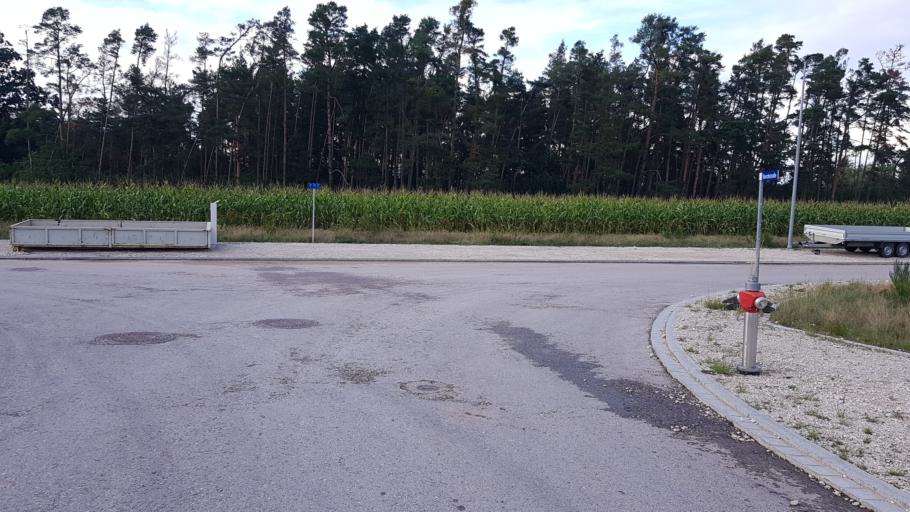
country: DE
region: Bavaria
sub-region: Regierungsbezirk Mittelfranken
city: Hilpoltstein
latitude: 49.1777
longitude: 11.1793
